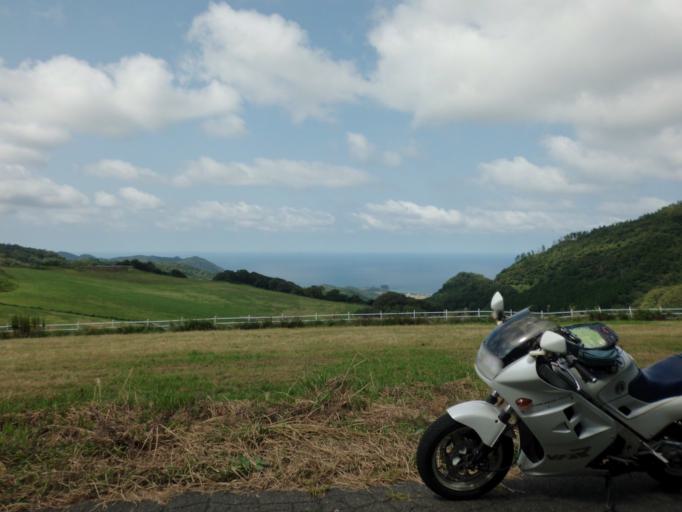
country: JP
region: Kyoto
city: Miyazu
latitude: 35.7256
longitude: 135.1975
